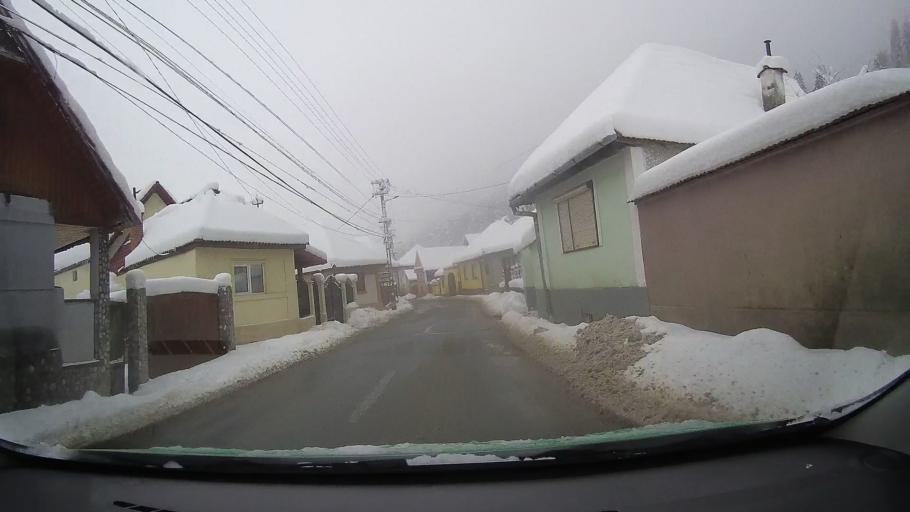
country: RO
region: Sibiu
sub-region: Comuna Tilisca
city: Tilisca
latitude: 45.7967
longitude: 23.8673
